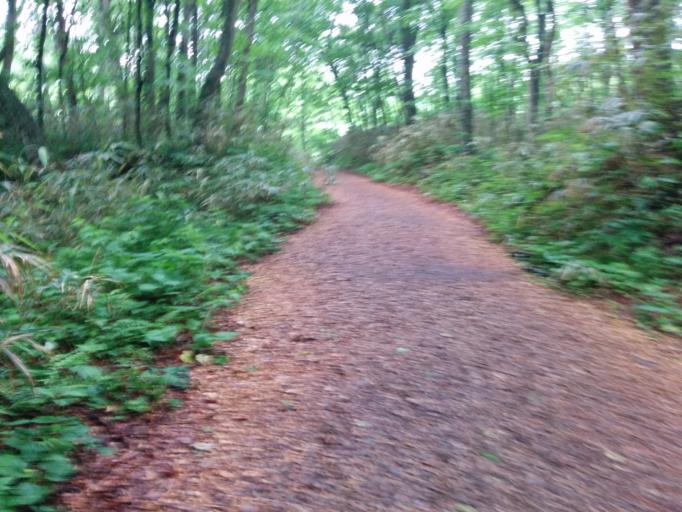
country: JP
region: Akita
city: Noshiromachi
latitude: 40.5615
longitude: 139.9823
